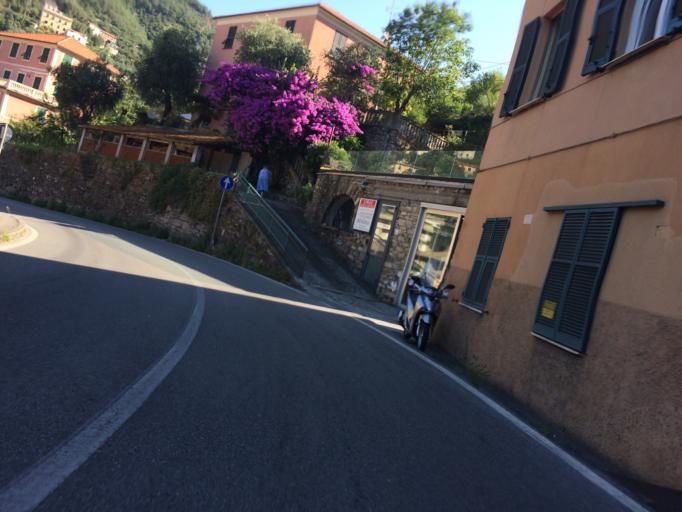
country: IT
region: Liguria
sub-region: Provincia di Genova
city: Zoagli
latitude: 44.3391
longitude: 9.2694
